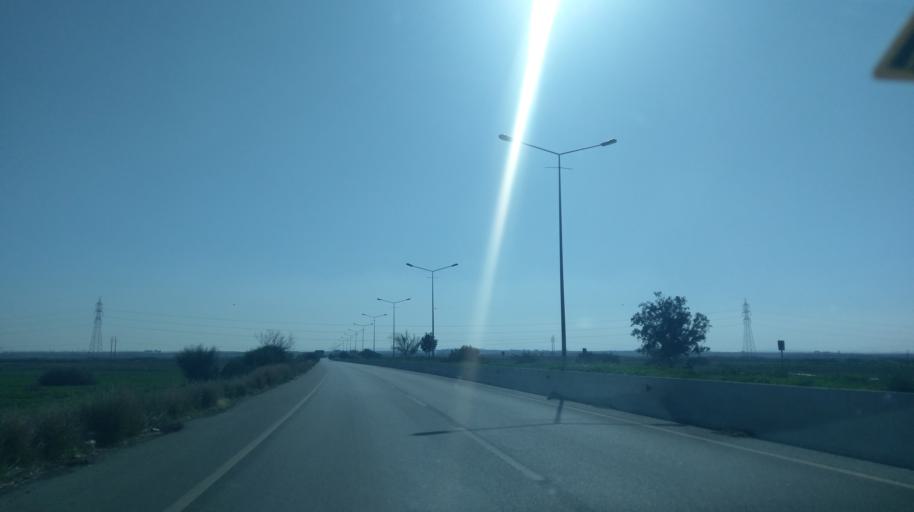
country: CY
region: Lefkosia
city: Geri
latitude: 35.1967
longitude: 33.5008
